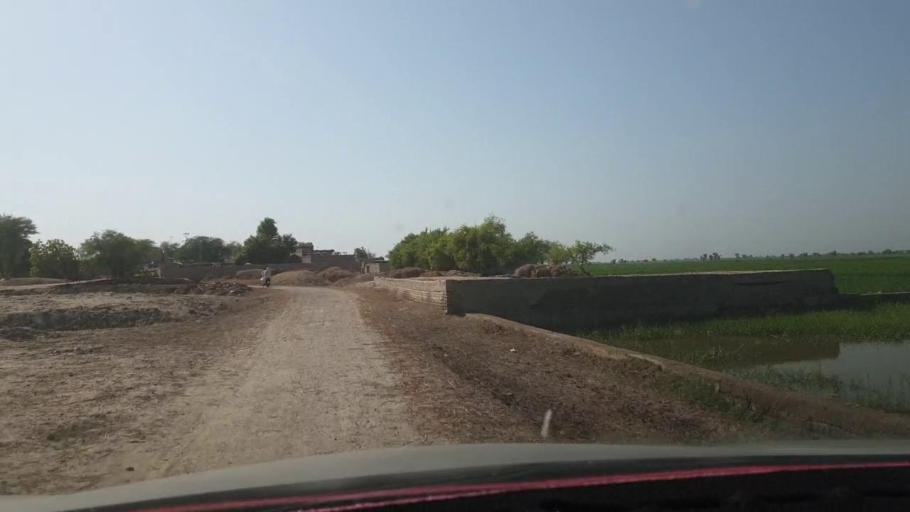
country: PK
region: Sindh
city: Nasirabad
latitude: 27.3847
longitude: 67.8736
